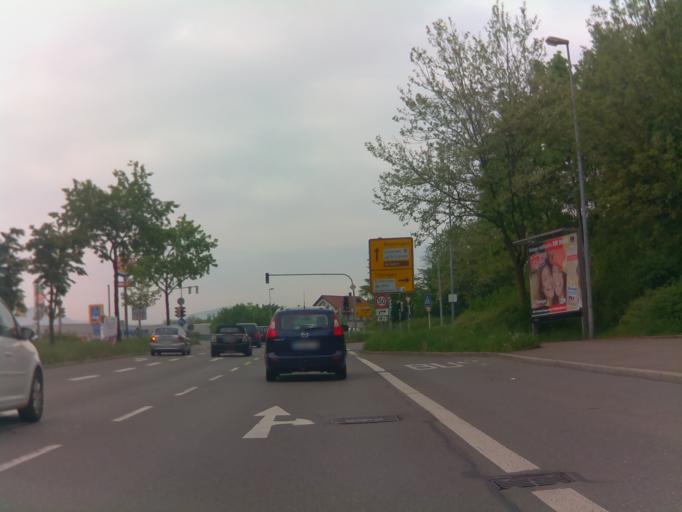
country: DE
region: Baden-Wuerttemberg
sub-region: Tuebingen Region
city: Reutlingen
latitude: 48.5031
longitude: 9.2059
